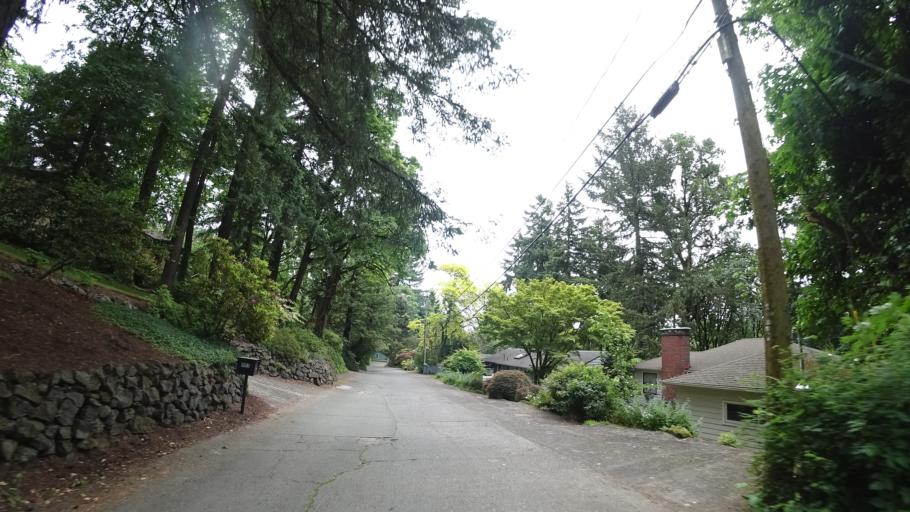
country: US
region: Oregon
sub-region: Multnomah County
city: Portland
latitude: 45.4809
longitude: -122.6886
